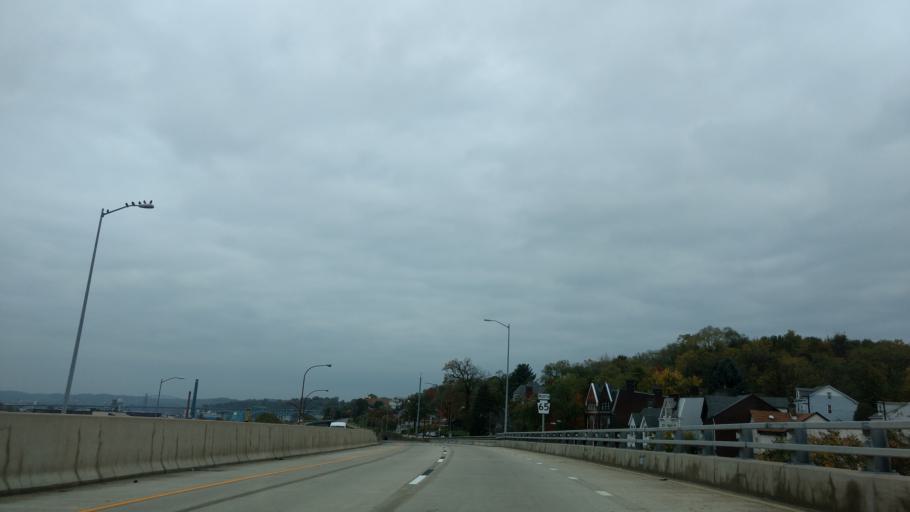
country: US
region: Pennsylvania
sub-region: Allegheny County
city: McKees Rocks
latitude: 40.4623
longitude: -80.0317
